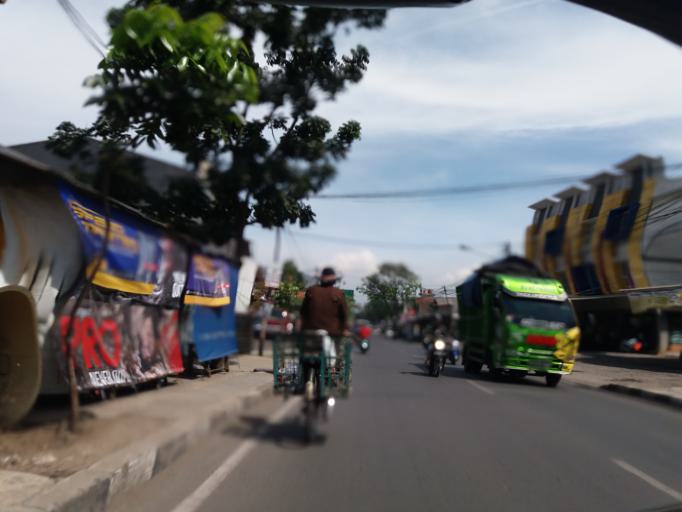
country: ID
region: West Java
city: Margahayukencana
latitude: -6.9384
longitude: 107.5696
